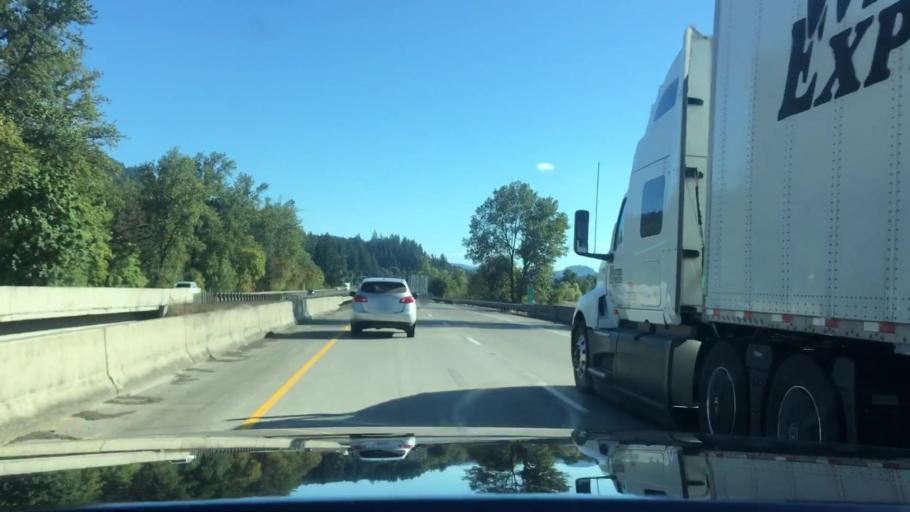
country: US
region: Oregon
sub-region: Lane County
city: Creswell
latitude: 43.8760
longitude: -123.0129
